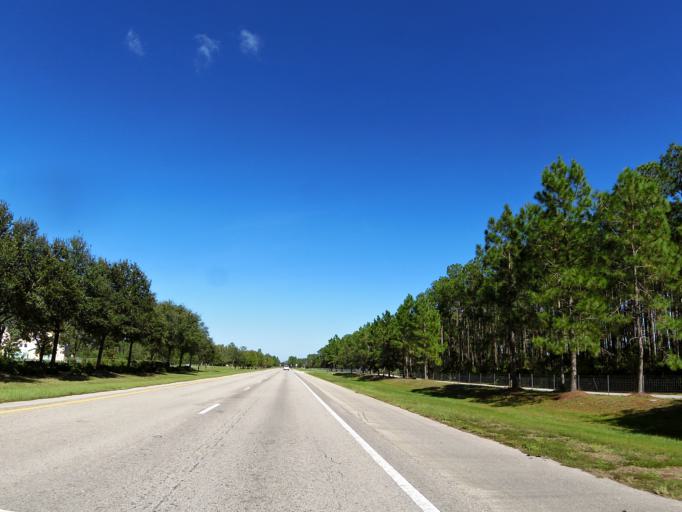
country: US
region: Florida
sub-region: Saint Johns County
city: Palm Valley
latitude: 30.1177
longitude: -81.4085
